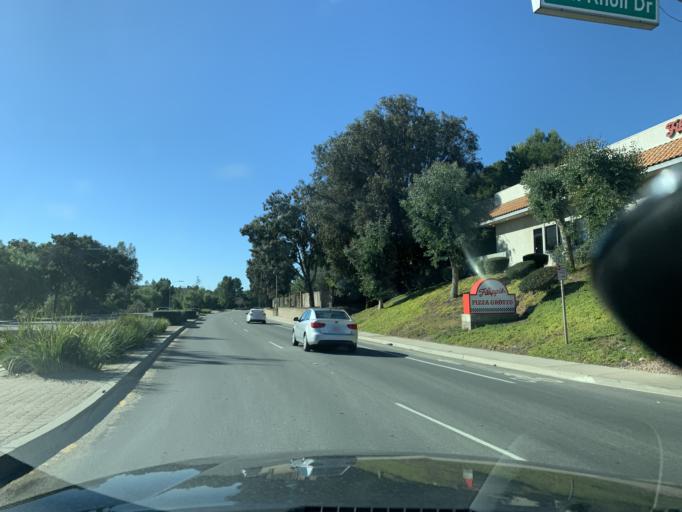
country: US
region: California
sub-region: San Diego County
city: Poway
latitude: 32.9508
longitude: -117.0677
